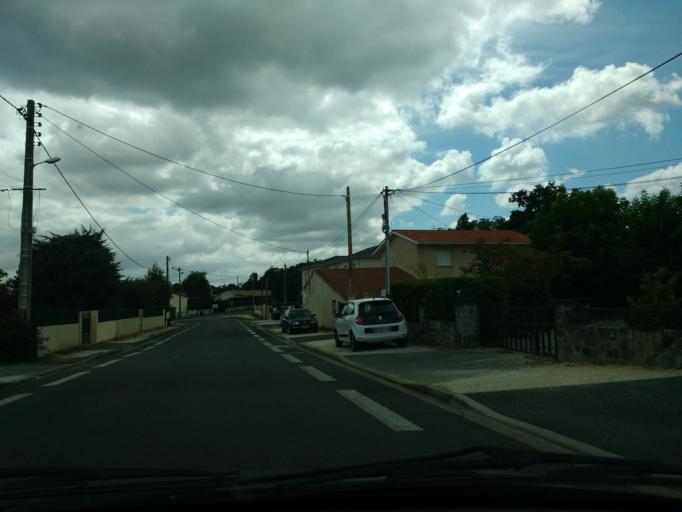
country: FR
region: Aquitaine
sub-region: Departement de la Gironde
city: Gradignan
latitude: 44.7758
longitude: -0.6009
